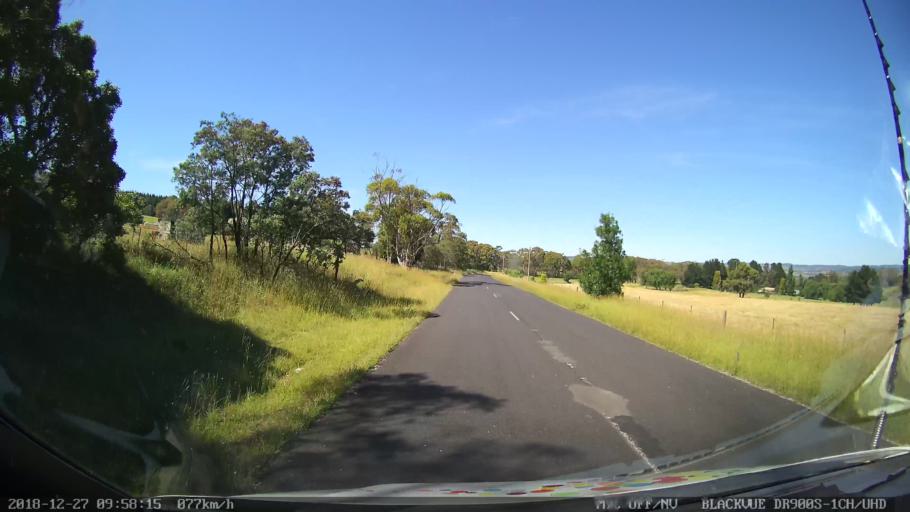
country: AU
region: New South Wales
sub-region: Lithgow
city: Portland
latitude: -33.4287
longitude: 149.9658
